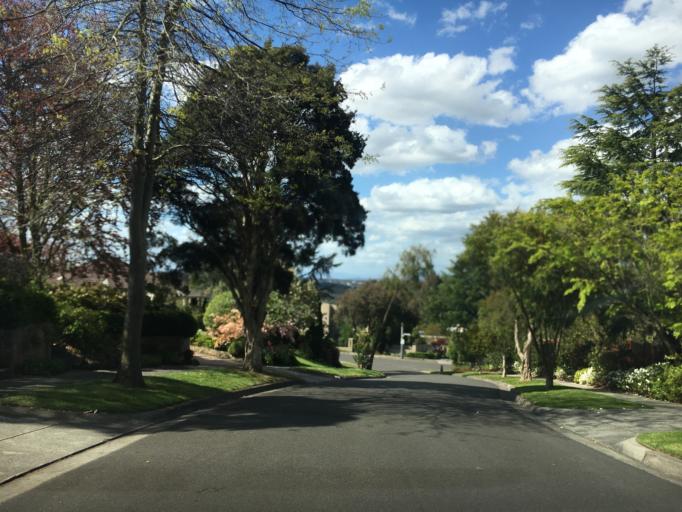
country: AU
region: Victoria
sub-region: Monash
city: Mulgrave
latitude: -37.8935
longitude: 145.1783
